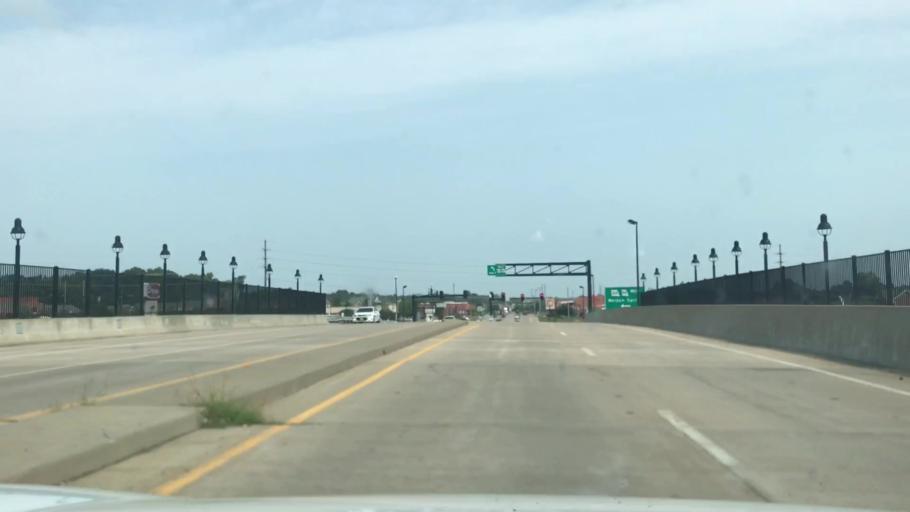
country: US
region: Missouri
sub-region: Saint Charles County
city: Cottleville
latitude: 38.7375
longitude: -90.6334
